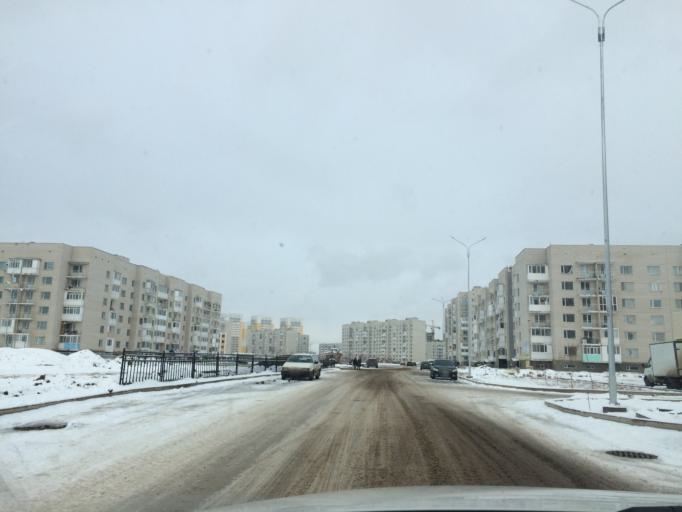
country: KZ
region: Astana Qalasy
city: Astana
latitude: 51.1216
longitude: 71.5041
